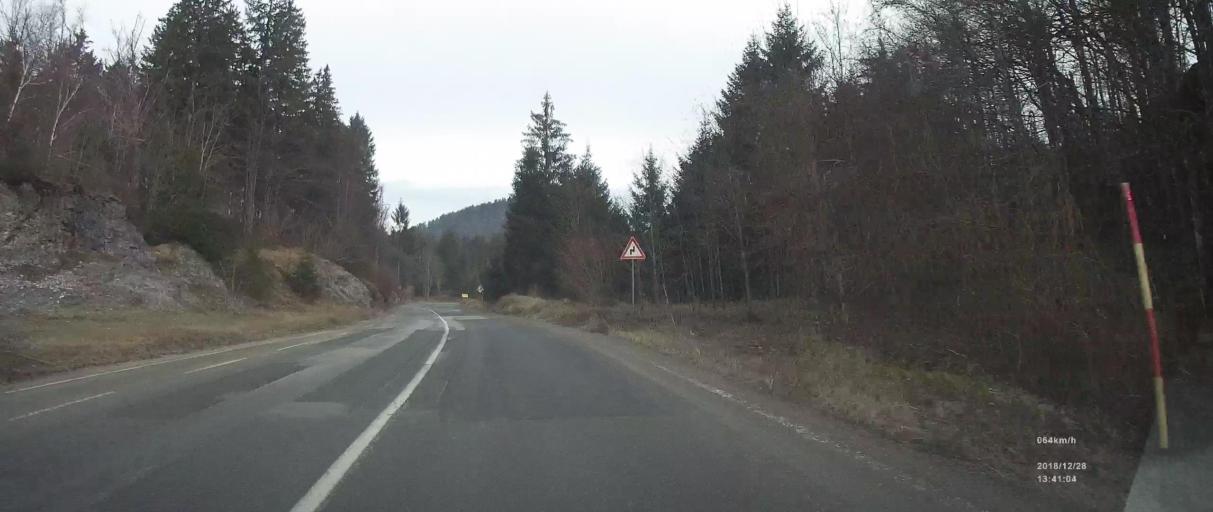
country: HR
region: Primorsko-Goranska
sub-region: Grad Delnice
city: Delnice
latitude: 45.3517
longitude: 14.7552
